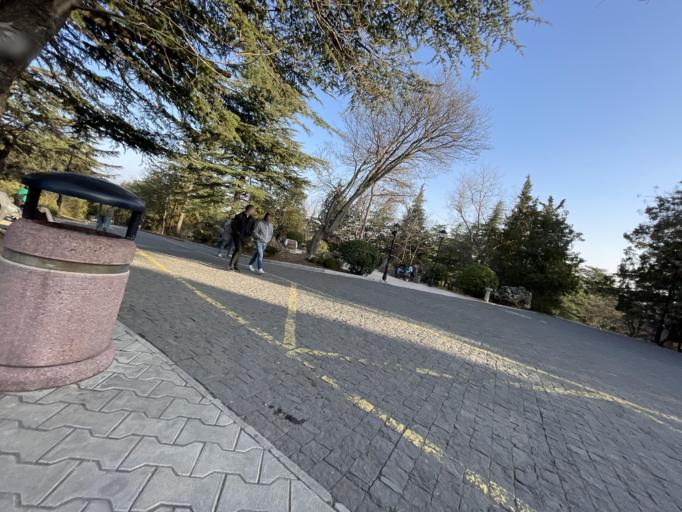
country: GE
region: T'bilisi
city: Tbilisi
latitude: 41.6944
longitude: 44.7840
